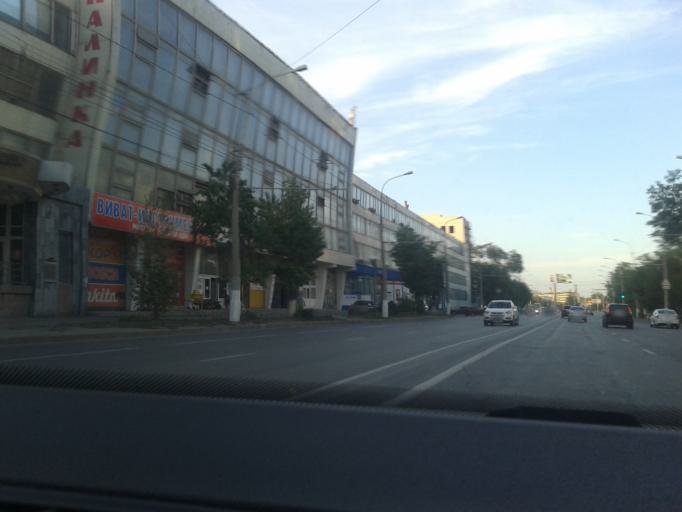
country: RU
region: Volgograd
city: Volgograd
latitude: 48.7327
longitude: 44.5418
